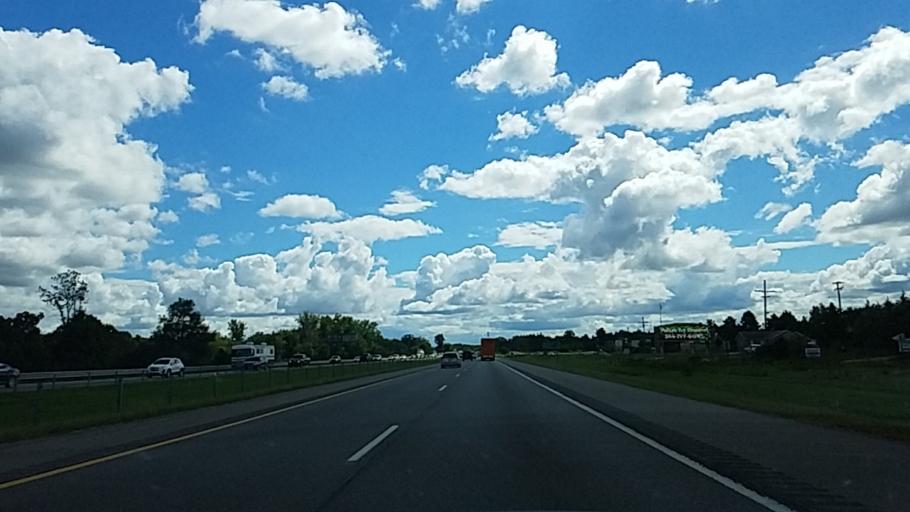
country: US
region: Michigan
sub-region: Livingston County
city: Brighton
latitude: 42.4945
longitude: -83.7577
